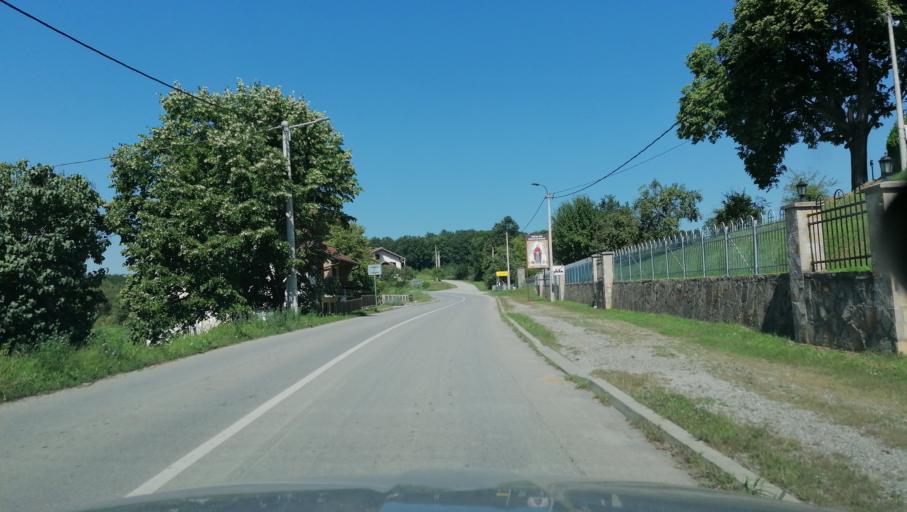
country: RS
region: Central Serbia
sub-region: Raski Okrug
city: Vrnjacka Banja
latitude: 43.7150
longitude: 20.8271
